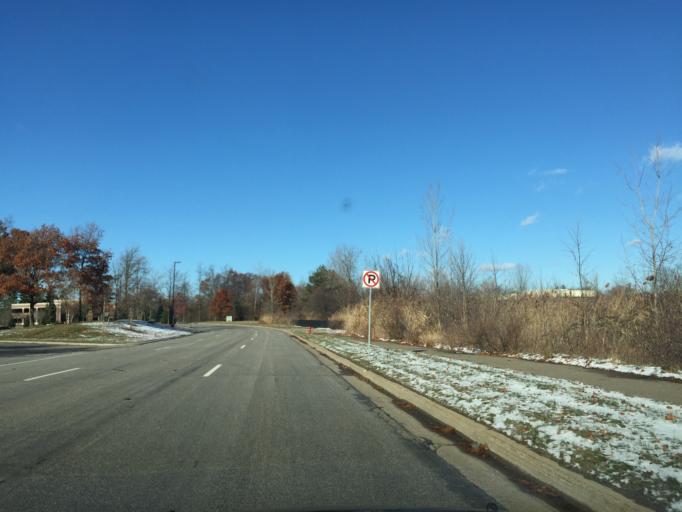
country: US
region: Michigan
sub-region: Oakland County
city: Auburn Hills
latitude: 42.6673
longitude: -83.2290
